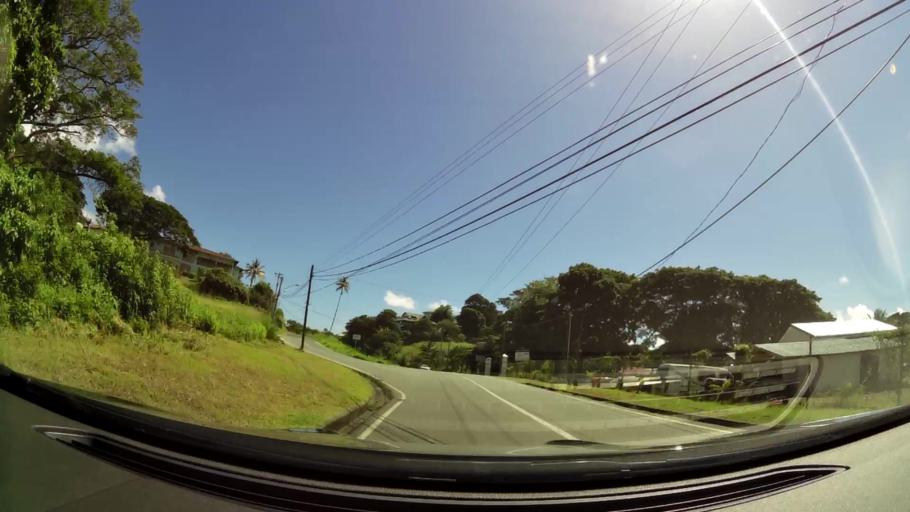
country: TT
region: Tobago
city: Scarborough
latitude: 11.1799
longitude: -60.7980
